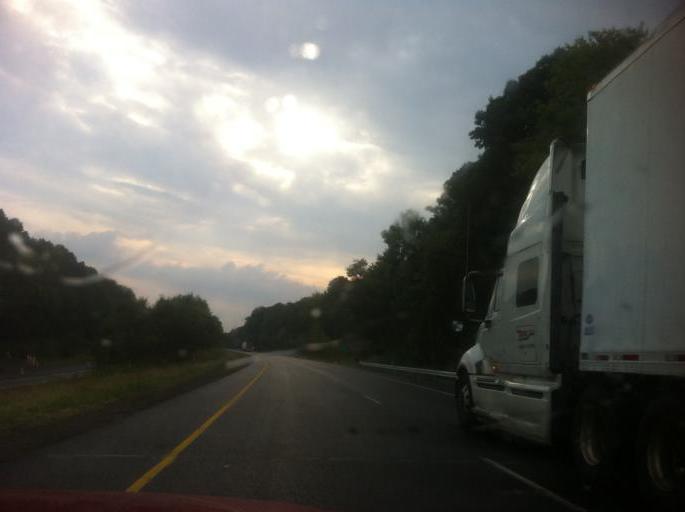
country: US
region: Pennsylvania
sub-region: Clarion County
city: Marianne
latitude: 41.1964
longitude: -79.4420
